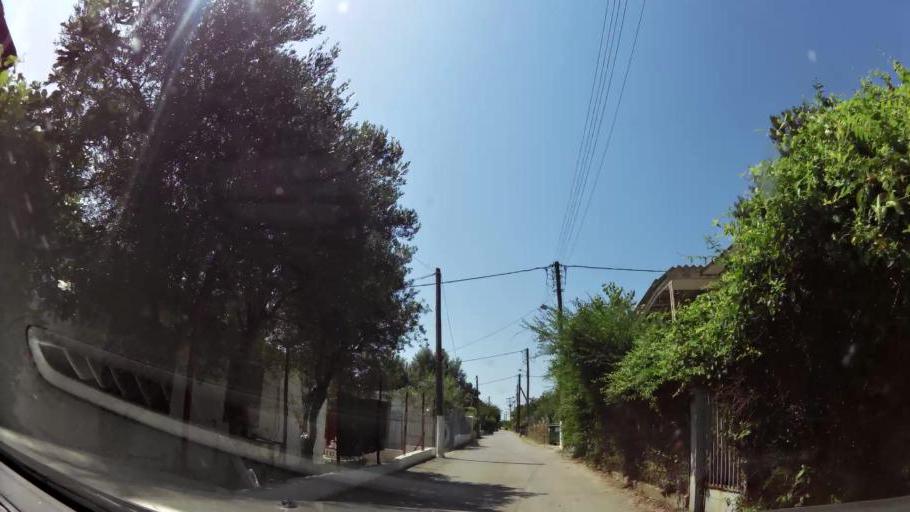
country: GR
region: Central Macedonia
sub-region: Nomos Thessalonikis
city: Neoi Epivates
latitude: 40.4968
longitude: 22.8941
